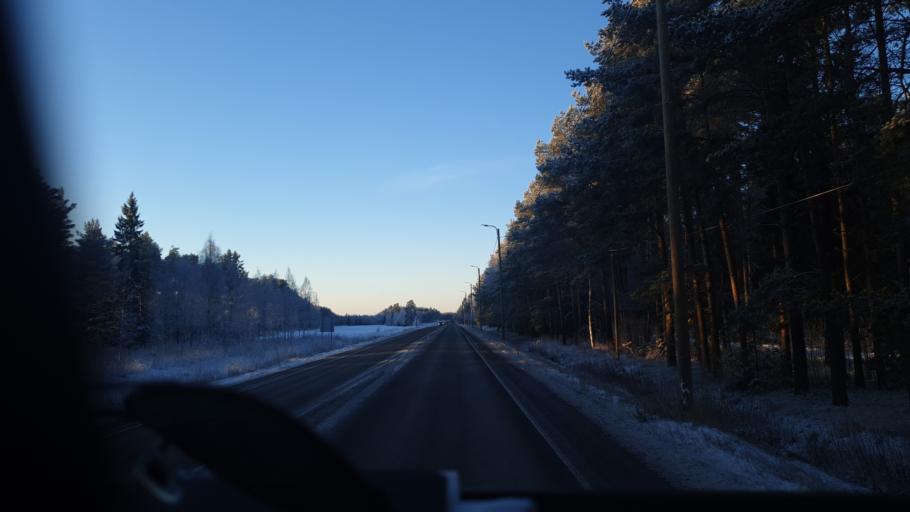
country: FI
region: Northern Ostrobothnia
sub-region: Ylivieska
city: Kalajoki
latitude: 64.2468
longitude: 23.8797
